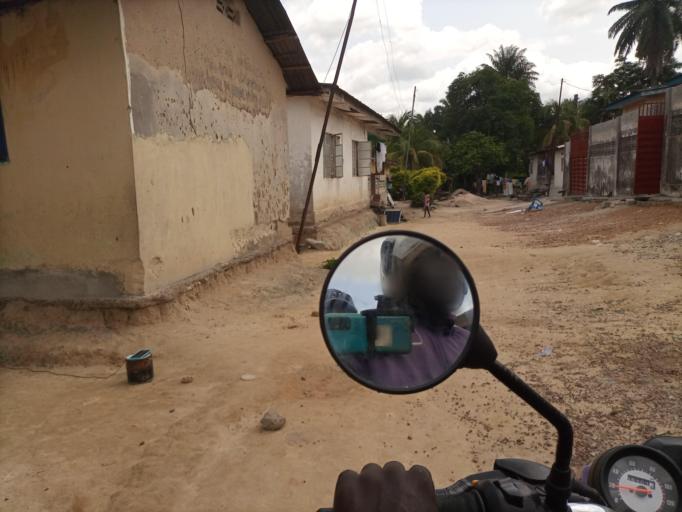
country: SL
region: Southern Province
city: Bo
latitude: 7.9490
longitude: -11.7349
